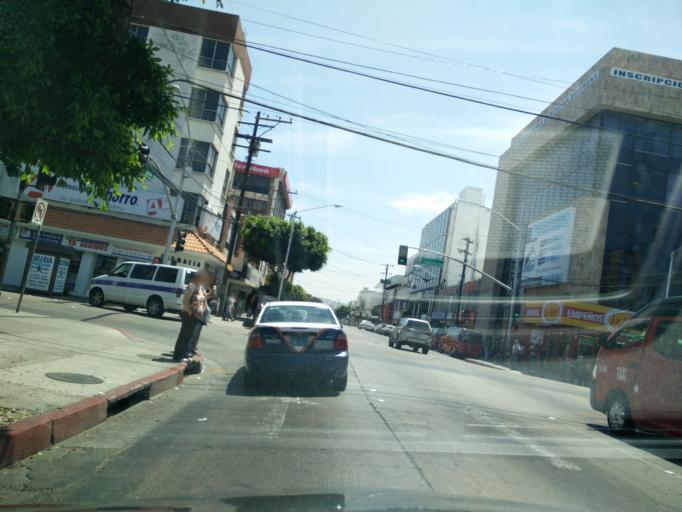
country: MX
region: Baja California
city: Tijuana
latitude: 32.5327
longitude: -117.0386
